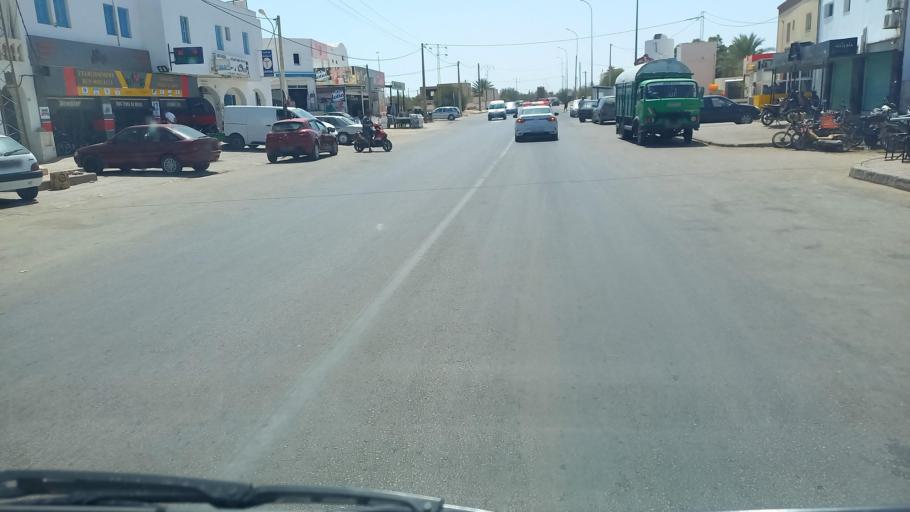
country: TN
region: Madanin
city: Houmt Souk
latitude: 33.7996
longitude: 10.8838
